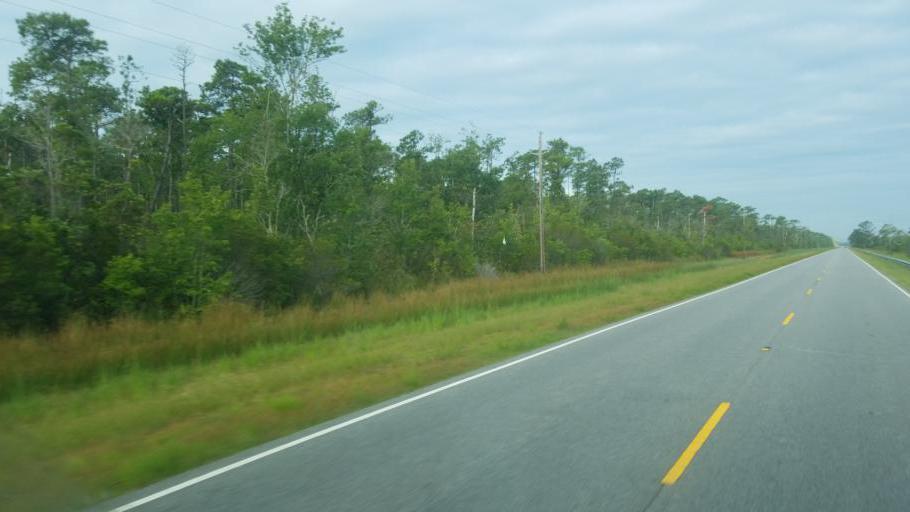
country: US
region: North Carolina
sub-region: Dare County
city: Manteo
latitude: 35.8695
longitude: -75.8026
